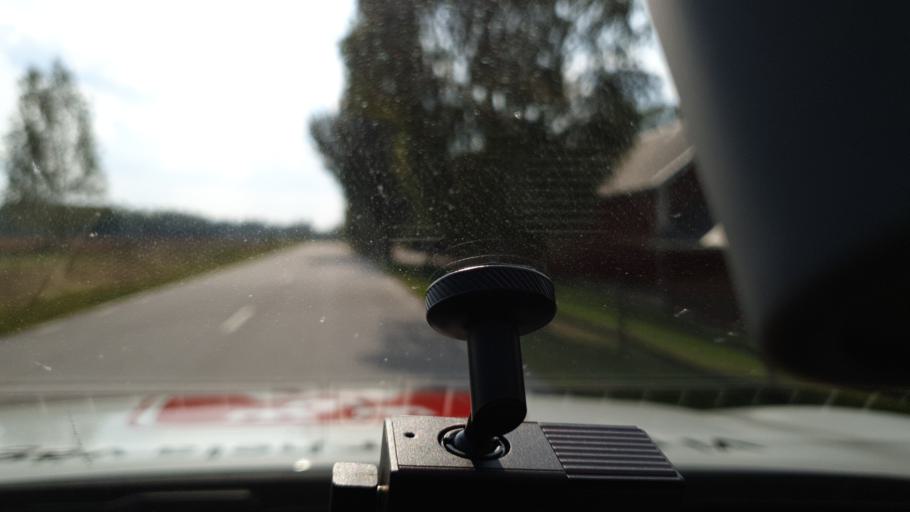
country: SE
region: Kalmar
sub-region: Vimmerby Kommun
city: Vimmerby
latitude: 57.7128
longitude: 15.8363
